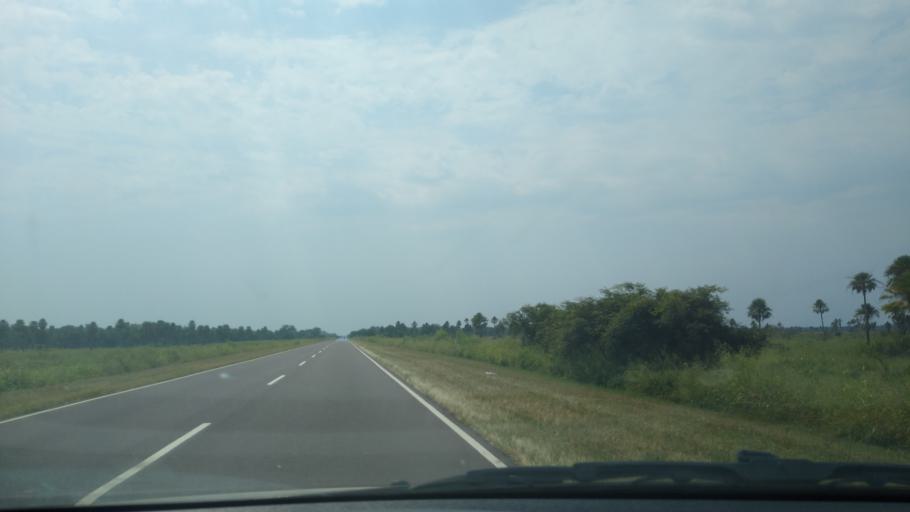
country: AR
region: Chaco
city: La Eduvigis
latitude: -27.0341
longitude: -58.9652
